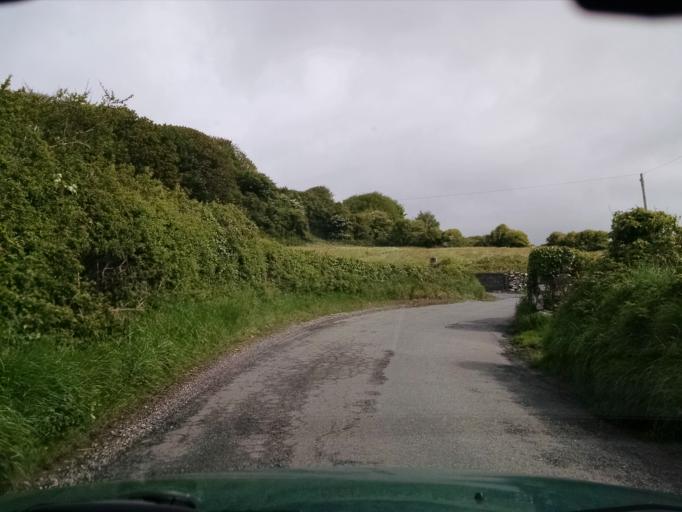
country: IE
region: Connaught
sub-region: County Galway
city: Bearna
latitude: 53.0435
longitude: -9.3451
